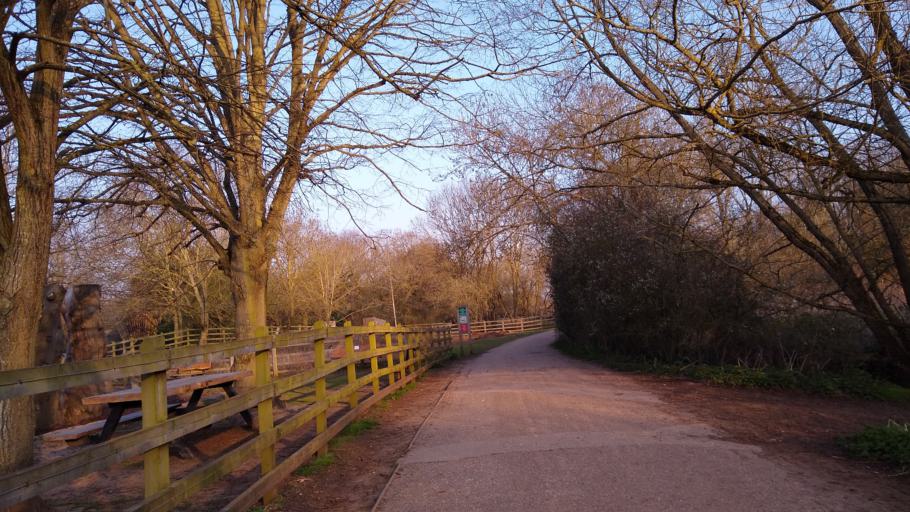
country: GB
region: England
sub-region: Wokingham
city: Woodley
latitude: 51.4409
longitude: -0.8750
